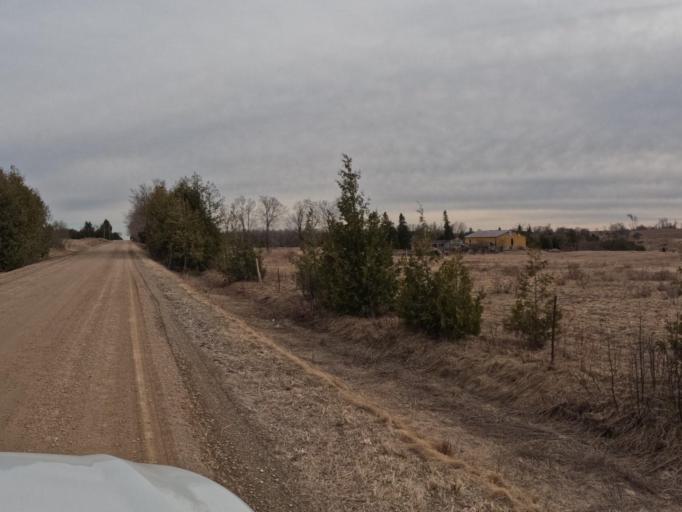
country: CA
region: Ontario
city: Shelburne
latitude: 43.9361
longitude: -80.2590
